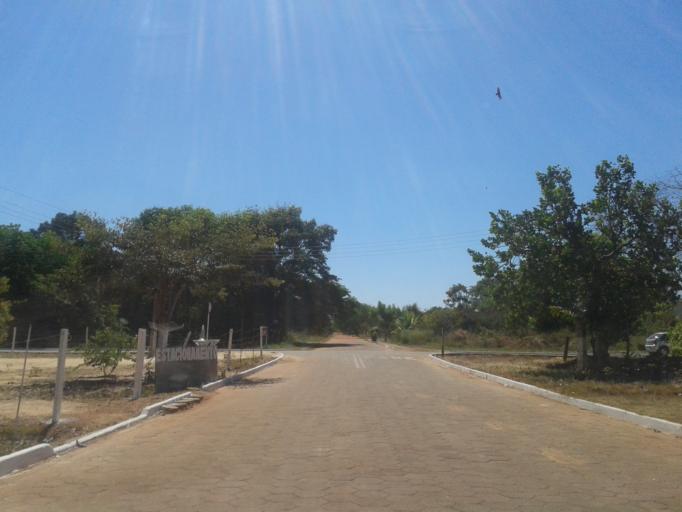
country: BR
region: Goias
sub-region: Sao Miguel Do Araguaia
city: Sao Miguel do Araguaia
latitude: -13.2168
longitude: -50.5771
